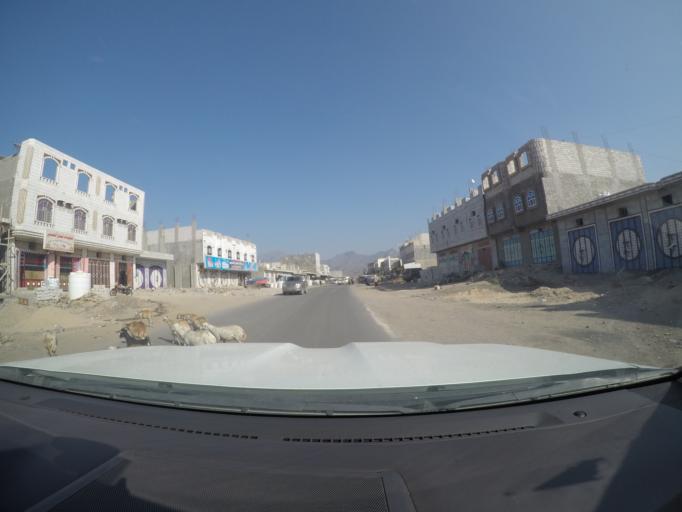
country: YE
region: Lahij
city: Habil ar Raydah
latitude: 13.6450
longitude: 44.8575
